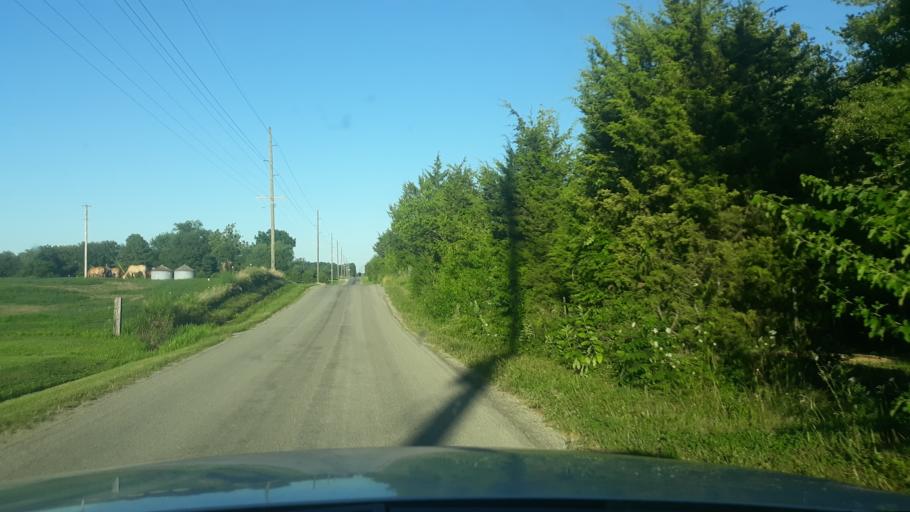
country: US
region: Illinois
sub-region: Saline County
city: Eldorado
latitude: 37.8630
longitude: -88.5509
